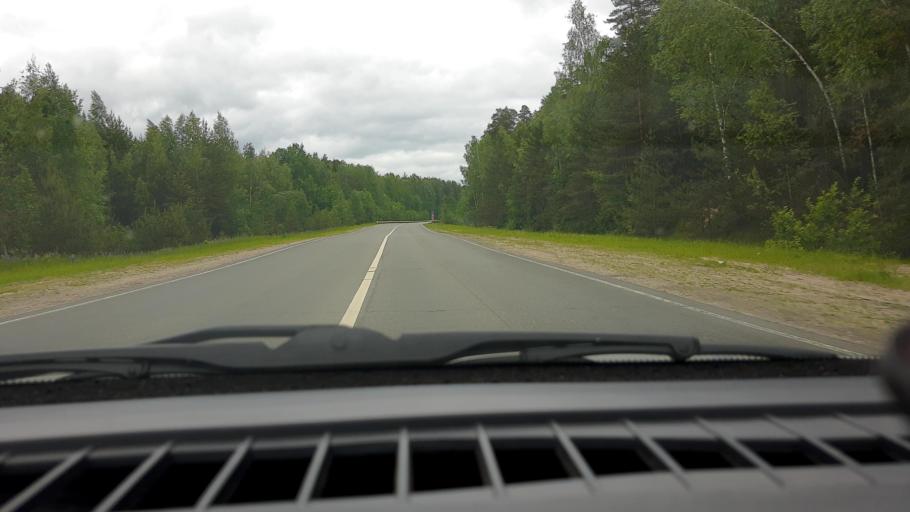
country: RU
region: Nizjnij Novgorod
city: Semenov
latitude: 56.8004
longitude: 44.4603
